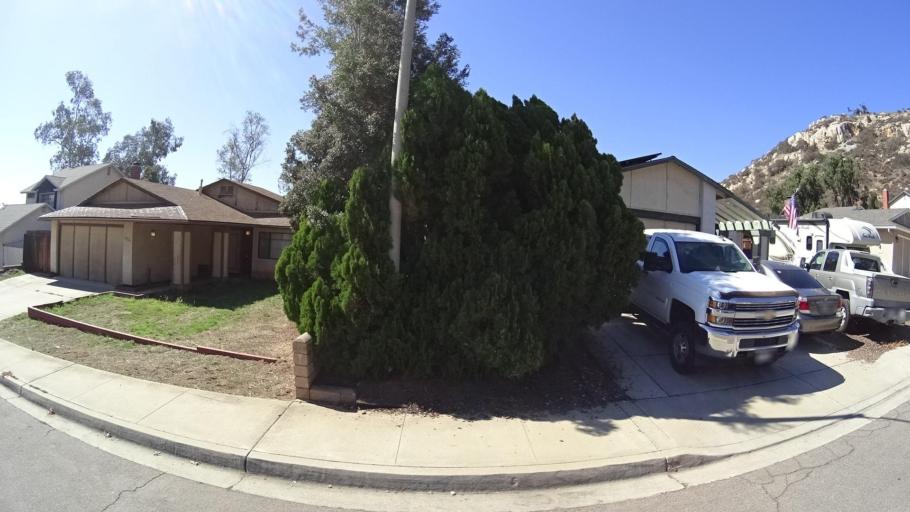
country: US
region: California
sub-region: San Diego County
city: Winter Gardens
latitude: 32.8291
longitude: -116.9524
